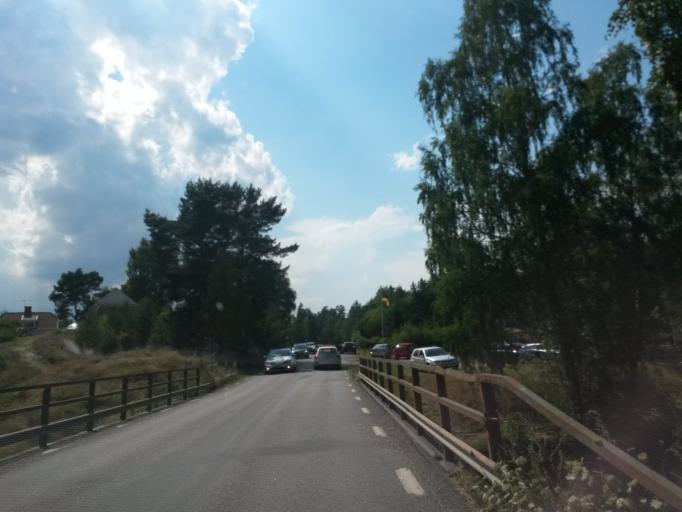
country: SE
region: Vaestra Goetaland
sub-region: Lidkopings Kommun
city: Lidkoping
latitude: 58.6269
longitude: 13.1363
